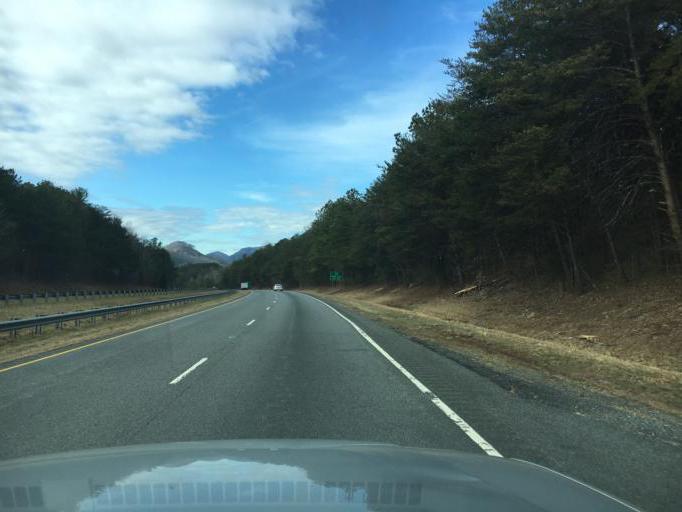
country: US
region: North Carolina
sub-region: Polk County
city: Columbus
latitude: 35.2702
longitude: -82.1605
